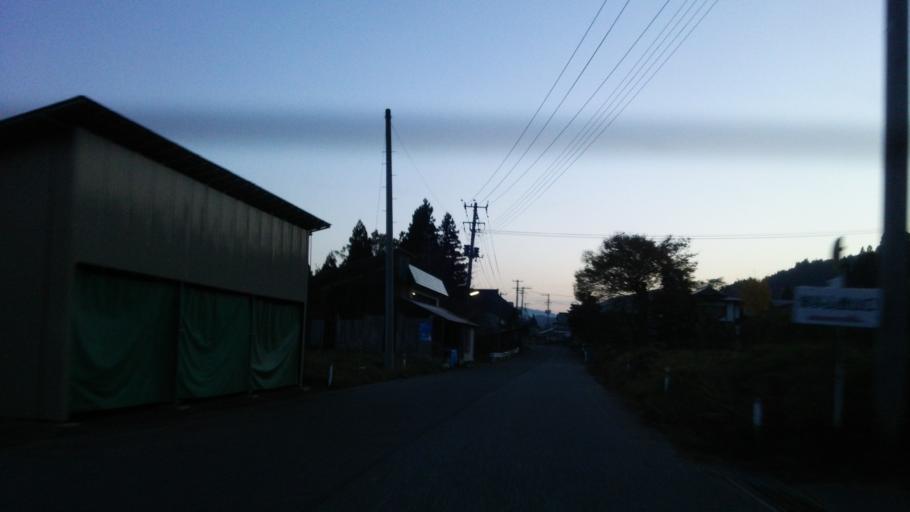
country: JP
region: Fukushima
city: Kitakata
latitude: 37.5251
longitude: 139.7120
